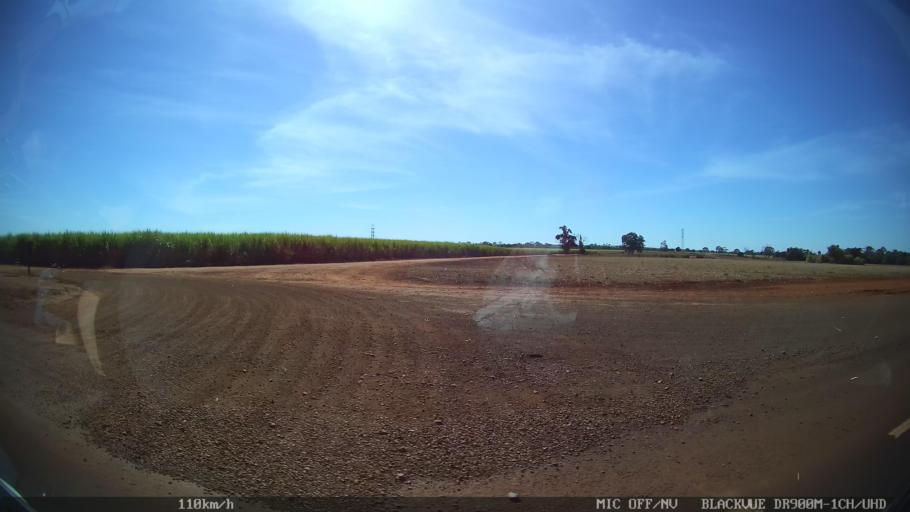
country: BR
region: Sao Paulo
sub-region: Guaira
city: Guaira
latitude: -20.4434
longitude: -48.3375
